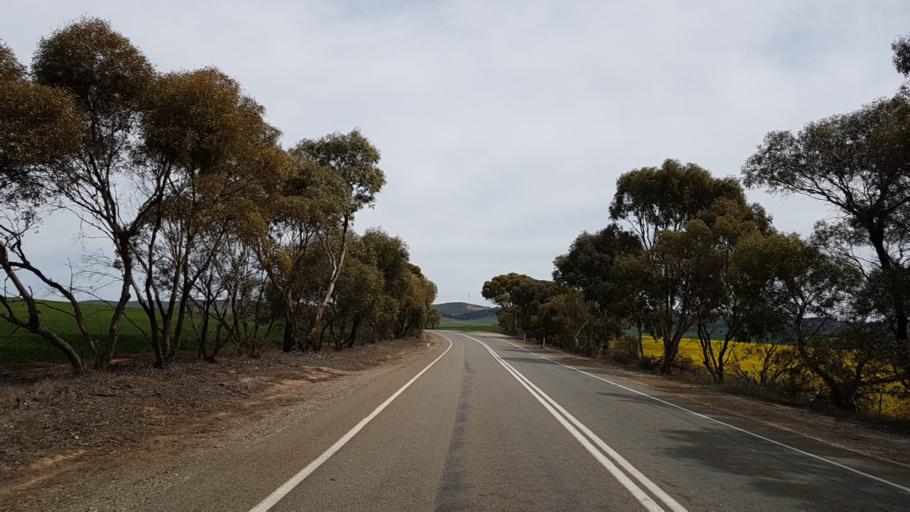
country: AU
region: South Australia
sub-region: Northern Areas
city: Jamestown
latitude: -33.0407
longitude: 138.6304
